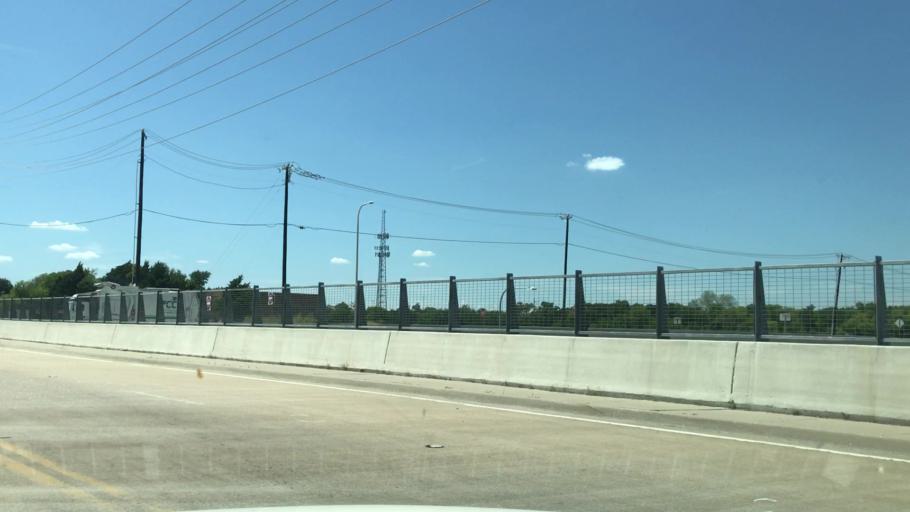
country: US
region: Texas
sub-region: Dallas County
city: Rowlett
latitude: 32.9036
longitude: -96.5557
